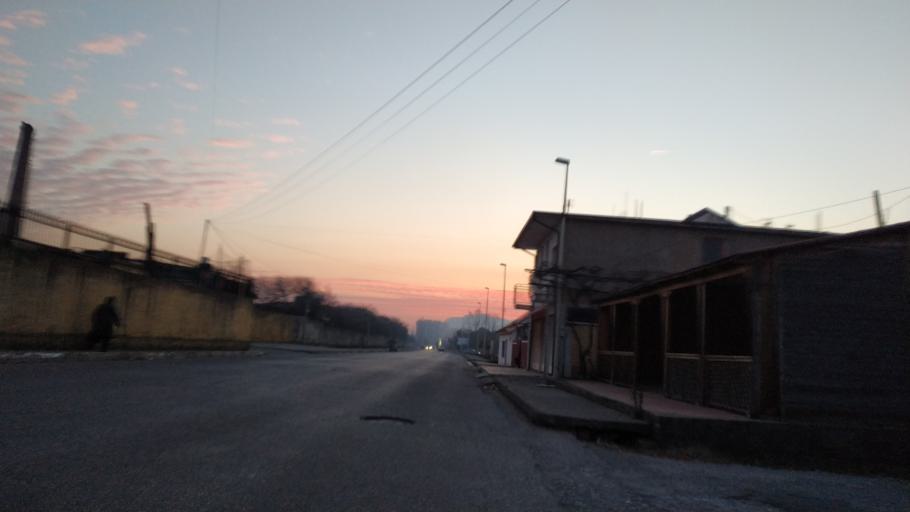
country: AL
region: Shkoder
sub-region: Rrethi i Shkodres
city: Shkoder
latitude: 42.0829
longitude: 19.5274
